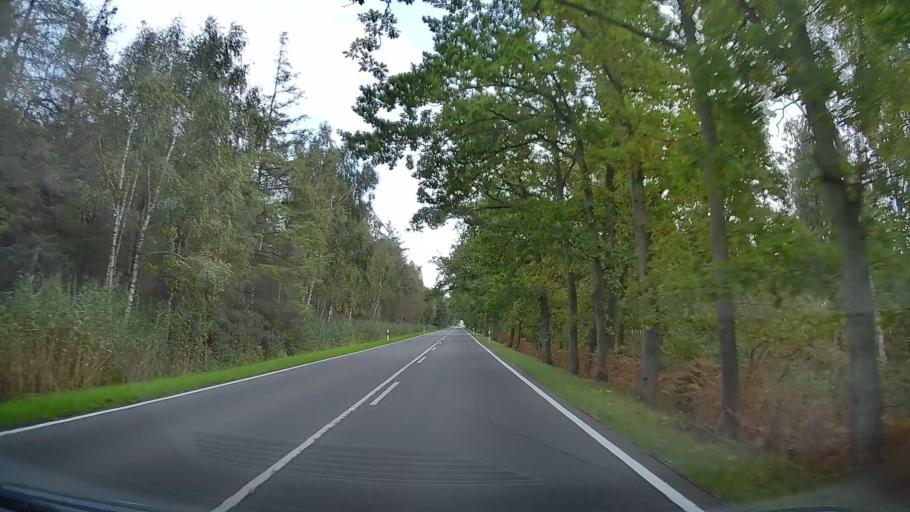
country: DE
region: Mecklenburg-Vorpommern
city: Zingst
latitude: 54.4202
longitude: 12.6537
